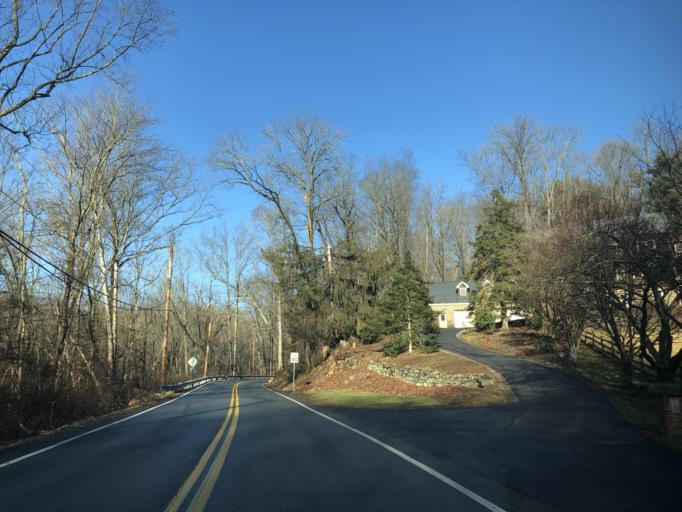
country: US
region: Pennsylvania
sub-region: Delaware County
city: Chester Heights
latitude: 39.9263
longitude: -75.4917
